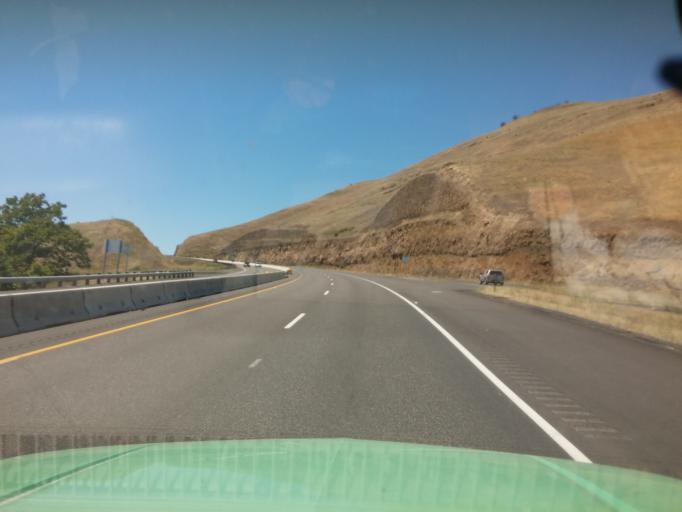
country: US
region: Idaho
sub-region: Nez Perce County
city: Lewiston
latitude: 46.4617
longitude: -116.9658
